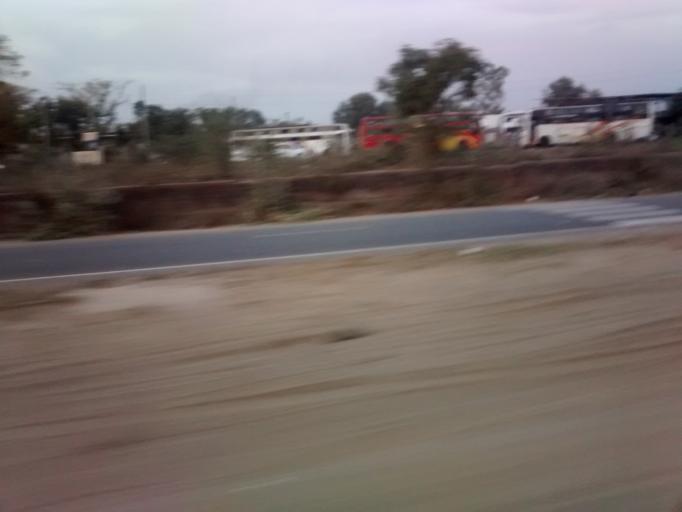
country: IN
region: Gujarat
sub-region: Ahmadabad
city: Naroda
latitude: 23.1141
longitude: 72.6647
